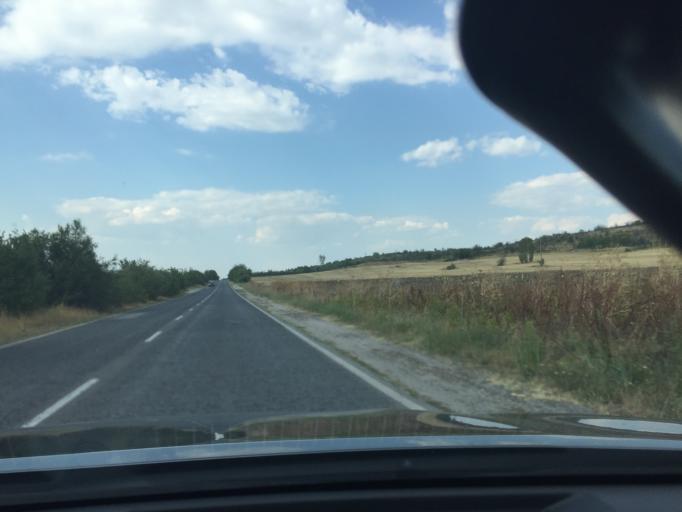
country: BG
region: Kyustendil
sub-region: Obshtina Boboshevo
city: Boboshevo
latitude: 42.1329
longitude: 23.0397
